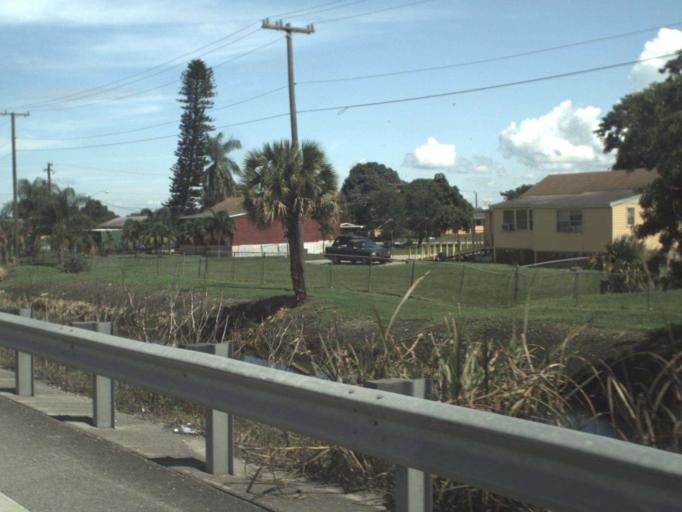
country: US
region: Florida
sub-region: Palm Beach County
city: Pahokee
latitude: 26.8062
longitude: -80.6533
